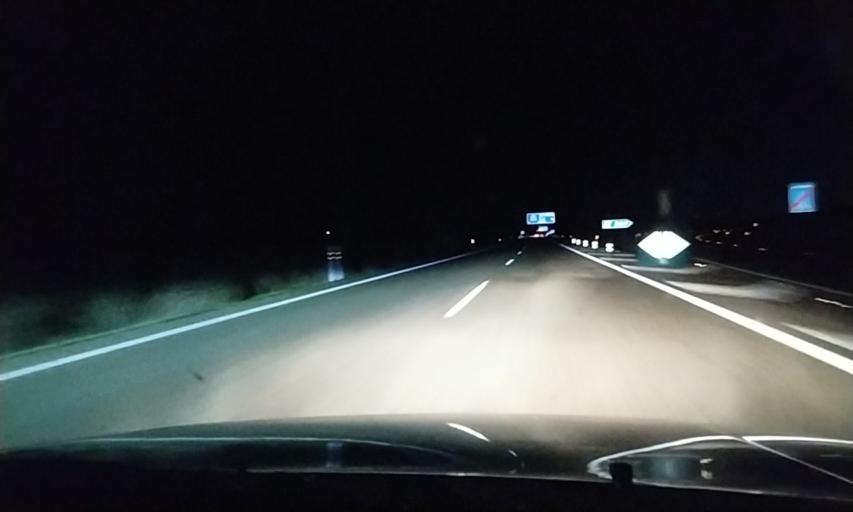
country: ES
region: Castille and Leon
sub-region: Provincia de Zamora
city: Villabrazaro
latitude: 42.0625
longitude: -5.6848
